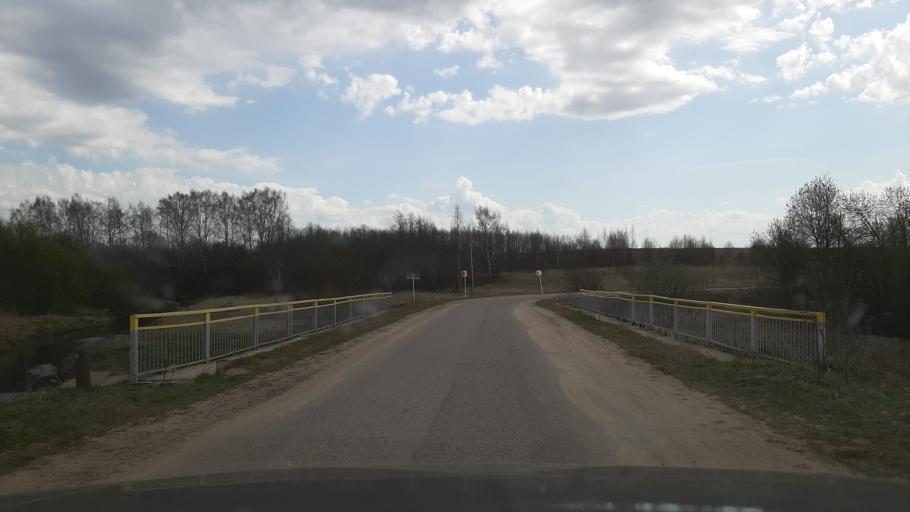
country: RU
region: Ivanovo
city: Furmanov
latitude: 57.3164
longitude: 41.1667
